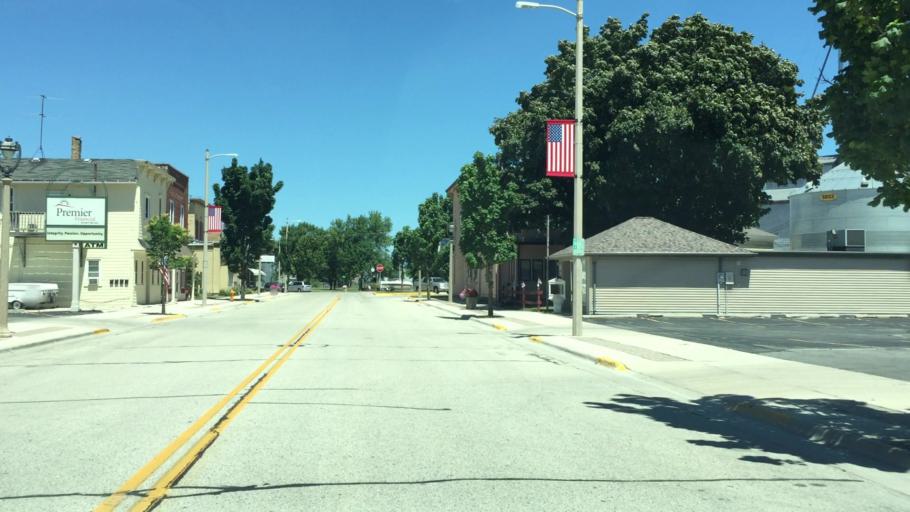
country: US
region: Wisconsin
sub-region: Calumet County
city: New Holstein
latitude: 43.9504
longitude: -88.0864
